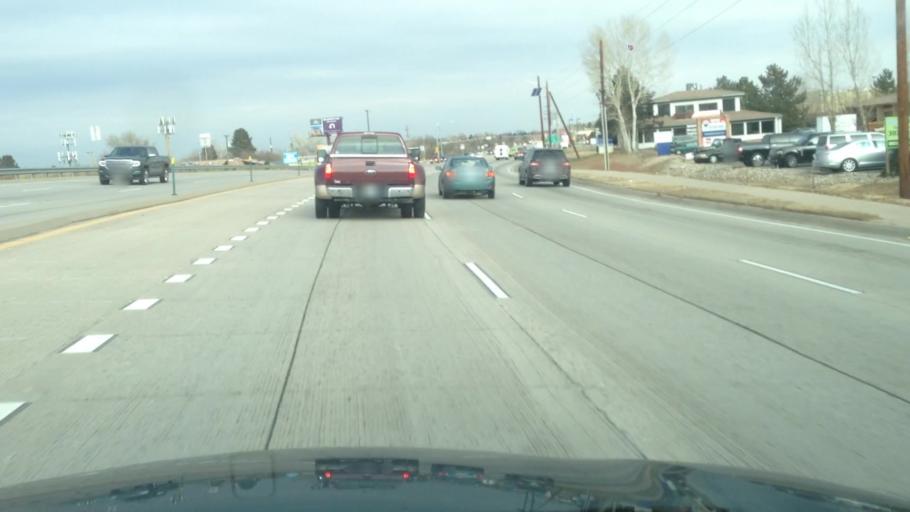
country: US
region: Colorado
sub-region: Arapahoe County
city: Dove Valley
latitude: 39.6352
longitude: -104.8287
